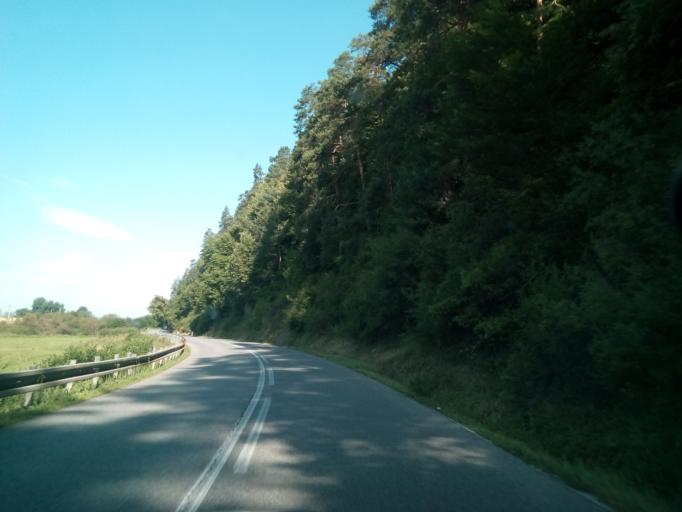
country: SK
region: Kosicky
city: Krompachy
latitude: 48.9357
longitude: 20.8353
